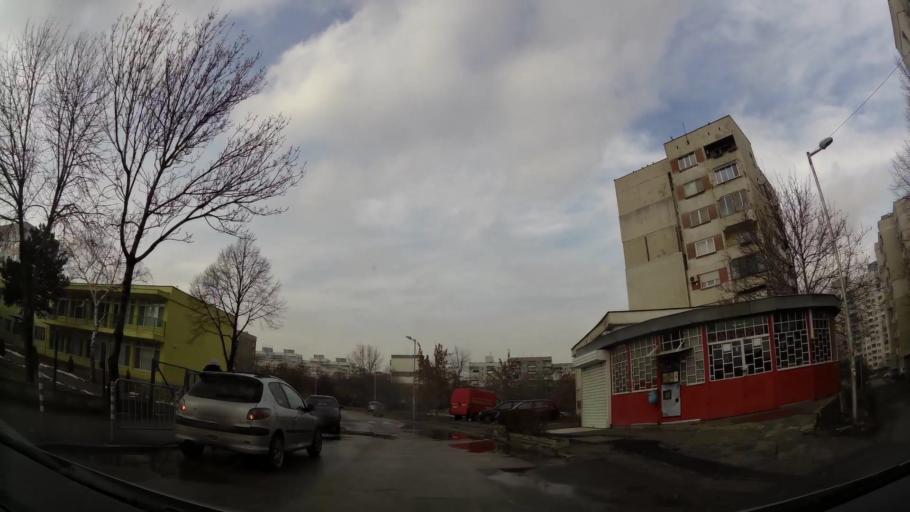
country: BG
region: Sofiya
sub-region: Obshtina Bozhurishte
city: Bozhurishte
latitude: 42.7212
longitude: 23.2473
